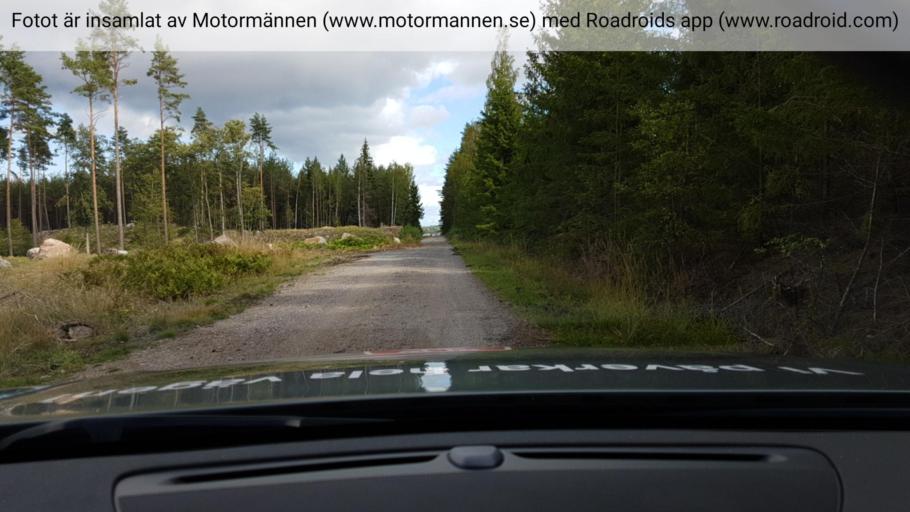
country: SE
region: Soedermanland
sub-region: Strangnas Kommun
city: Stallarholmen
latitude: 59.3536
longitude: 17.2612
